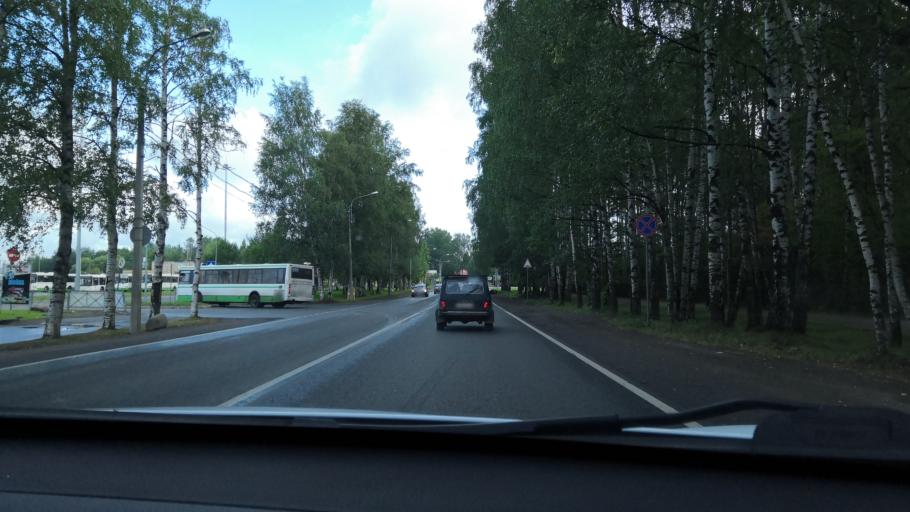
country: RU
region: St.-Petersburg
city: Pavlovsk
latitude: 59.6965
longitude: 30.4397
